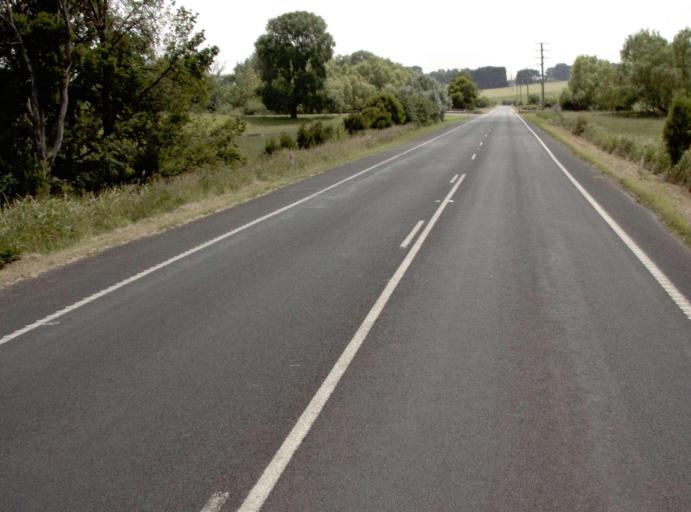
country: AU
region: Victoria
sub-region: Baw Baw
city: Warragul
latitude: -38.4572
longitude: 145.9727
